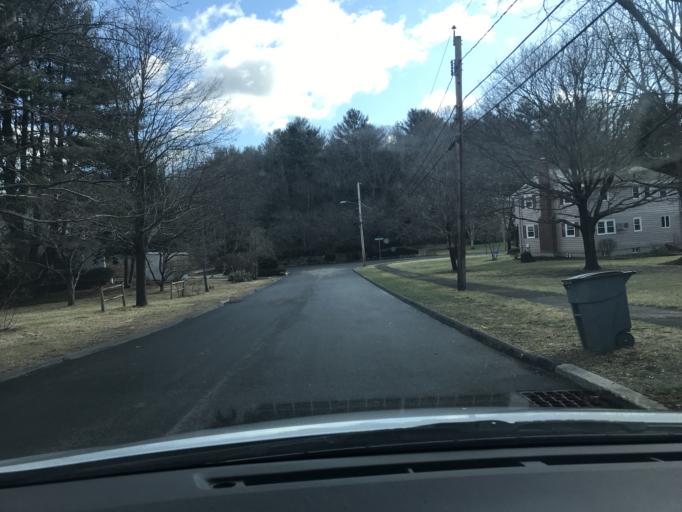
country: US
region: Massachusetts
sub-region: Middlesex County
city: Lexington
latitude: 42.4701
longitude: -71.2240
